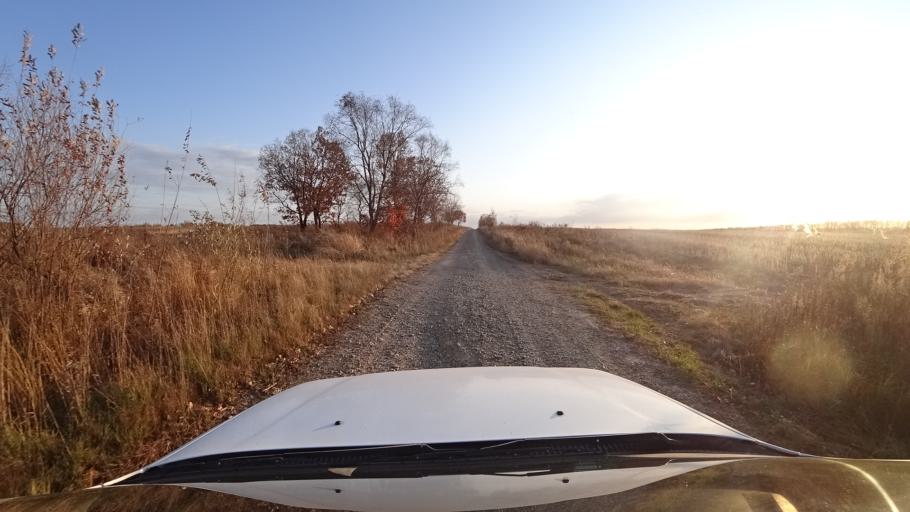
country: RU
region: Primorskiy
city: Lazo
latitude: 45.8141
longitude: 133.6100
